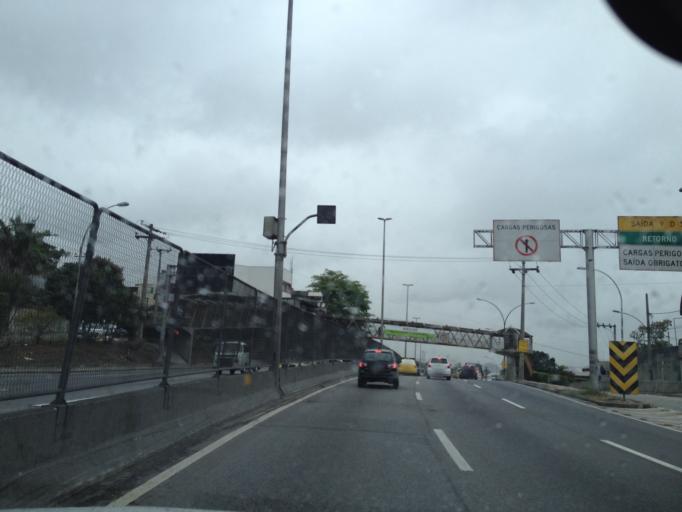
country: BR
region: Rio de Janeiro
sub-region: Rio De Janeiro
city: Rio de Janeiro
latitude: -22.8715
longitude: -43.2476
